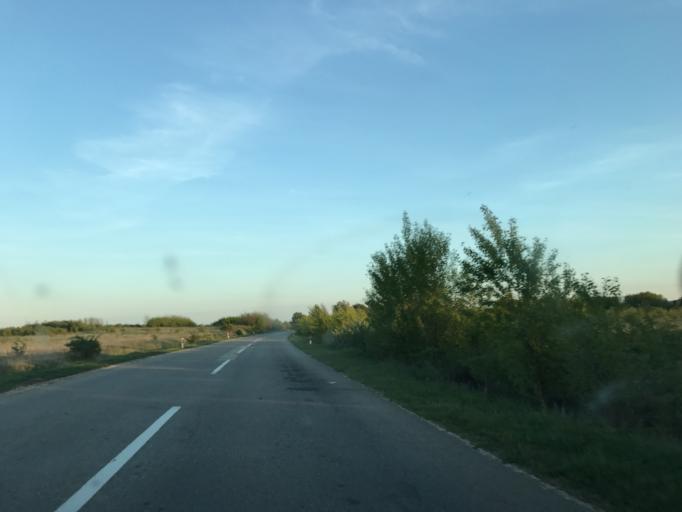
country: RO
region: Mehedinti
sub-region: Comuna Gogosu
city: Ostrovu Mare
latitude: 44.3803
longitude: 22.4783
